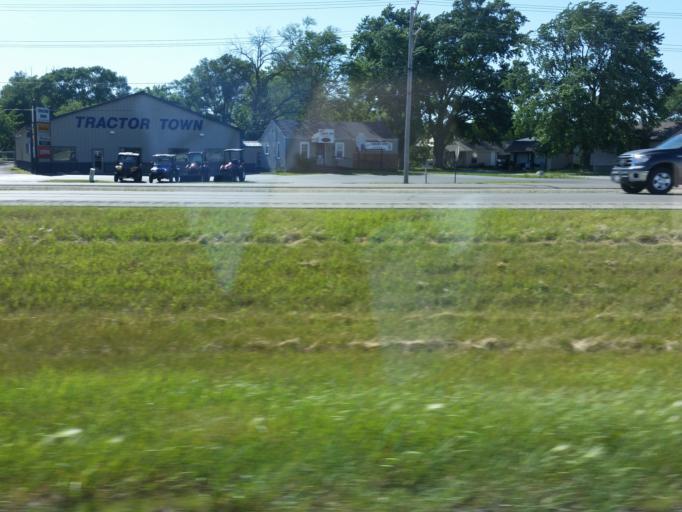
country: US
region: Illinois
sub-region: Winnebago County
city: Roscoe
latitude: 42.3845
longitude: -89.0199
